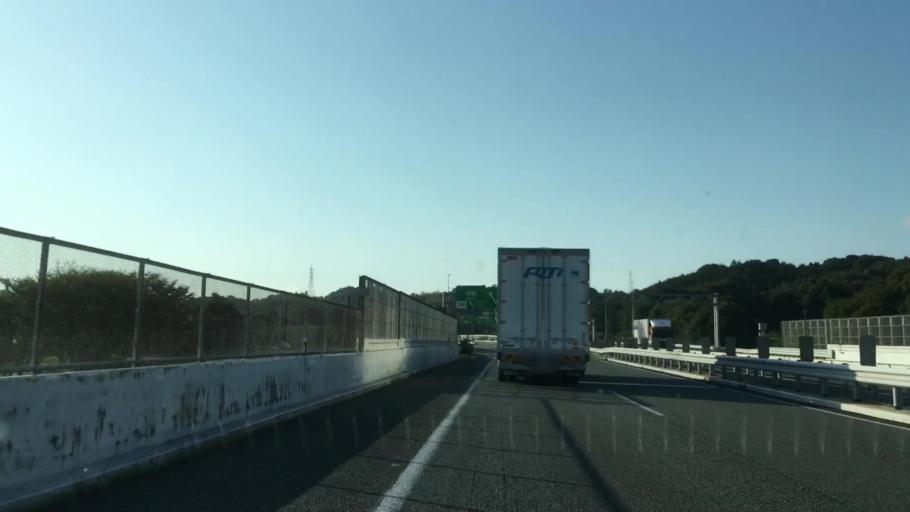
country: JP
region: Yamaguchi
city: Ogori-shimogo
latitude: 34.1244
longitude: 131.4088
